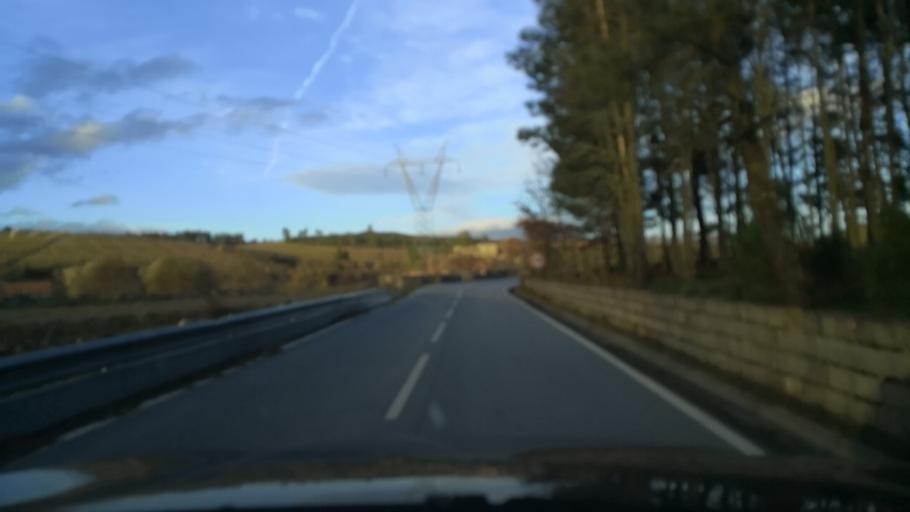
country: PT
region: Braganca
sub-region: Carrazeda de Ansiaes
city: Carrazeda de Anciaes
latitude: 41.2117
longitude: -7.3278
